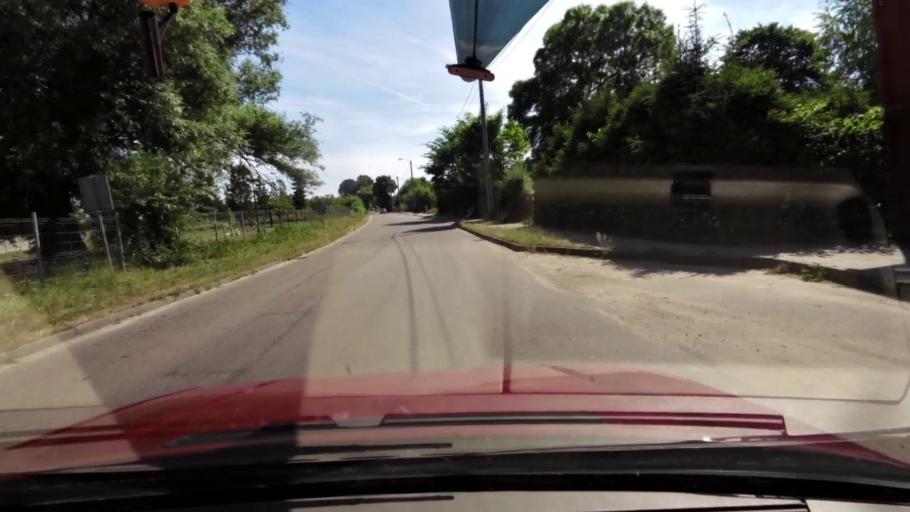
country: PL
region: Pomeranian Voivodeship
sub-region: Powiat slupski
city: Kobylnica
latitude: 54.3526
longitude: 16.9679
